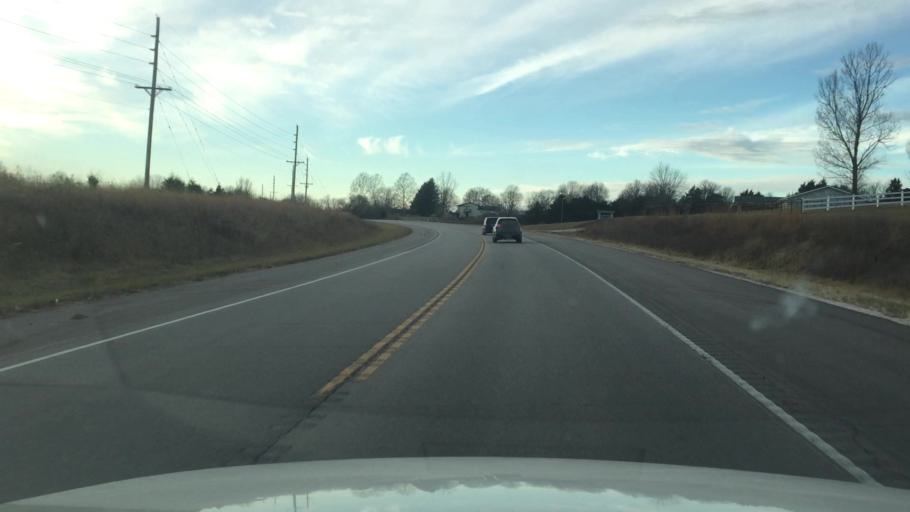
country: US
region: Missouri
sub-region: Miller County
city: Eldon
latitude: 38.3732
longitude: -92.6217
